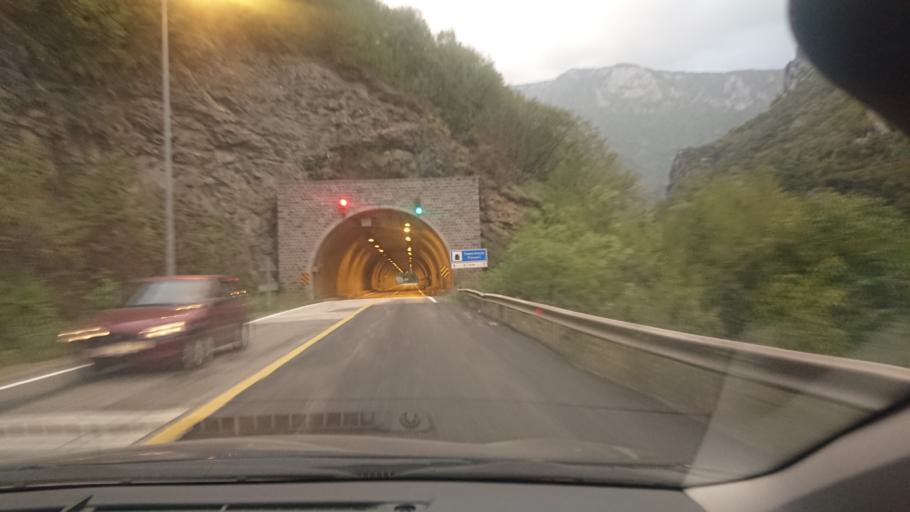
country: TR
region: Karabuk
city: Yenice
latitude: 41.1596
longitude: 32.4774
